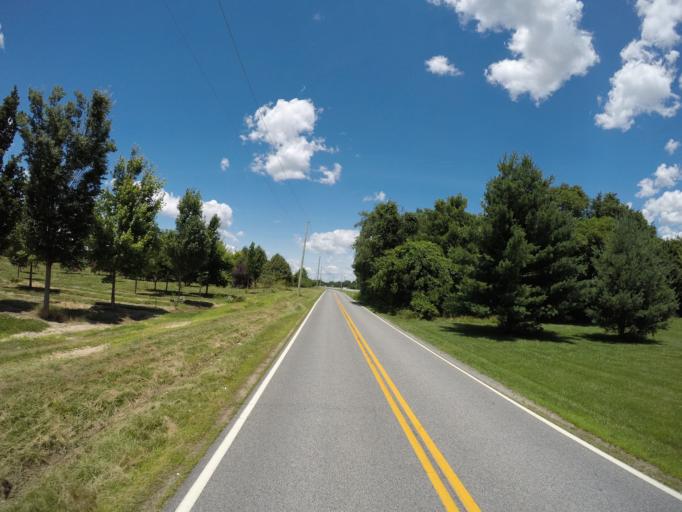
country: US
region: Delaware
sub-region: New Castle County
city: Middletown
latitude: 39.4787
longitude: -75.7783
